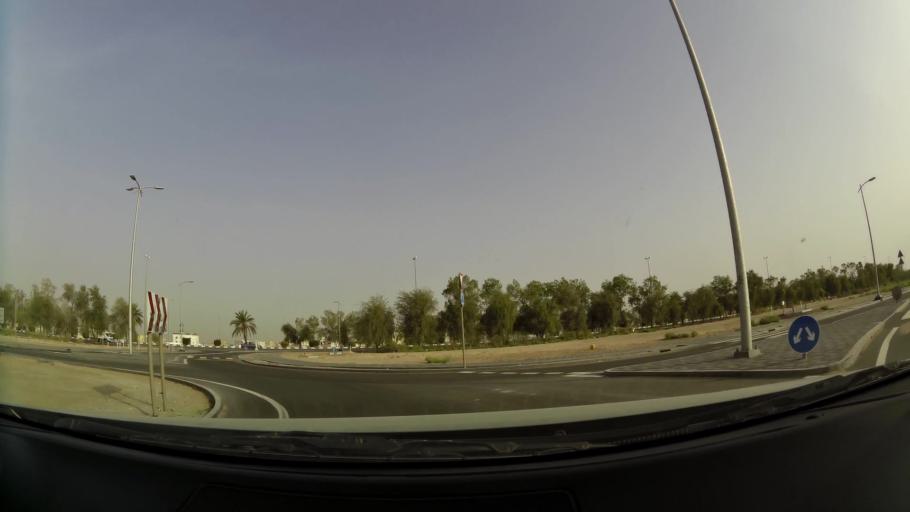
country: AE
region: Abu Dhabi
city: Al Ain
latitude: 24.1059
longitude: 55.6973
